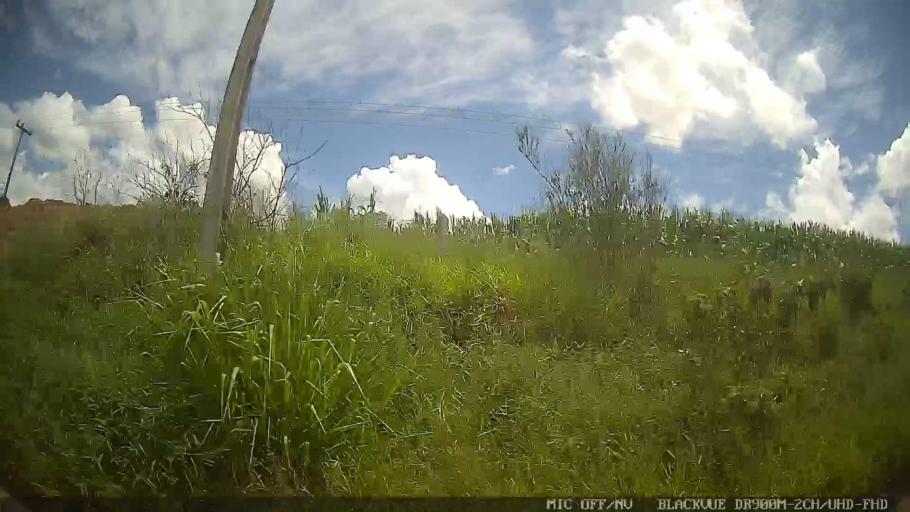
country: BR
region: Minas Gerais
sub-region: Extrema
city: Extrema
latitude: -22.7267
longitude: -46.3901
